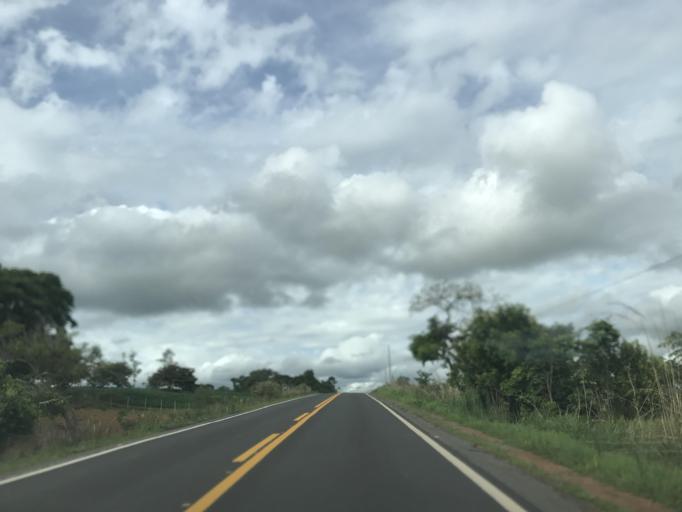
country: BR
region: Goias
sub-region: Bela Vista De Goias
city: Bela Vista de Goias
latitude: -17.1911
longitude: -48.6953
